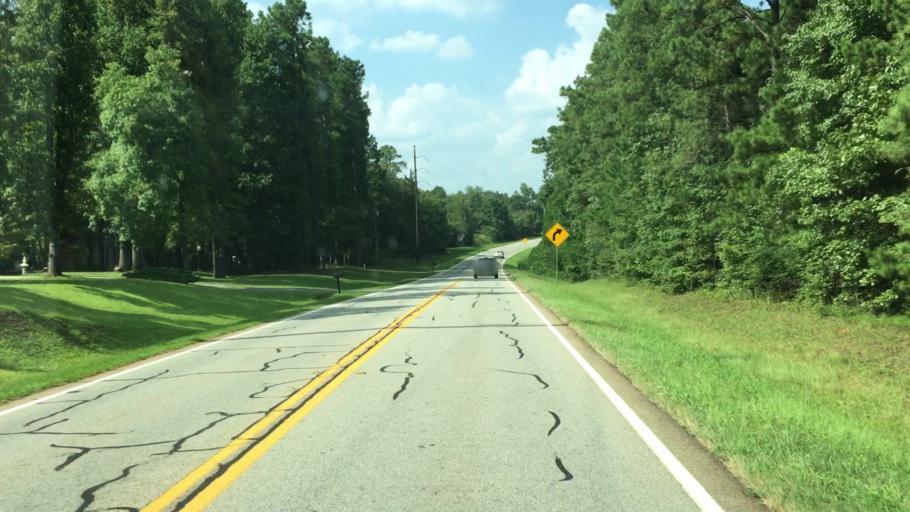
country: US
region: Georgia
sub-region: Jasper County
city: Monticello
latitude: 33.2806
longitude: -83.7134
